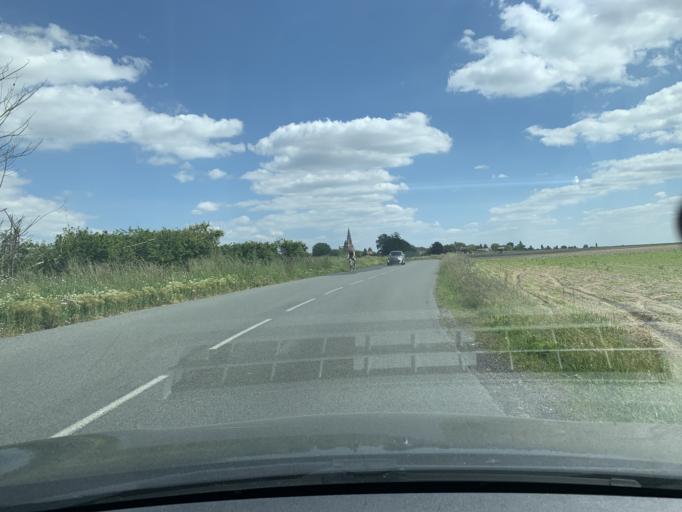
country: FR
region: Nord-Pas-de-Calais
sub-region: Departement du Pas-de-Calais
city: Oisy-le-Verger
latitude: 50.2566
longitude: 3.1100
